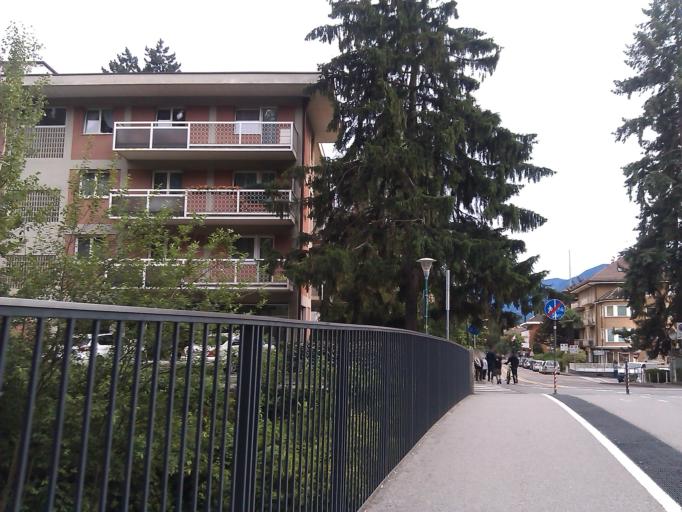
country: IT
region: Trentino-Alto Adige
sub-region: Bolzano
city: Merano
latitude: 46.6694
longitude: 11.1562
